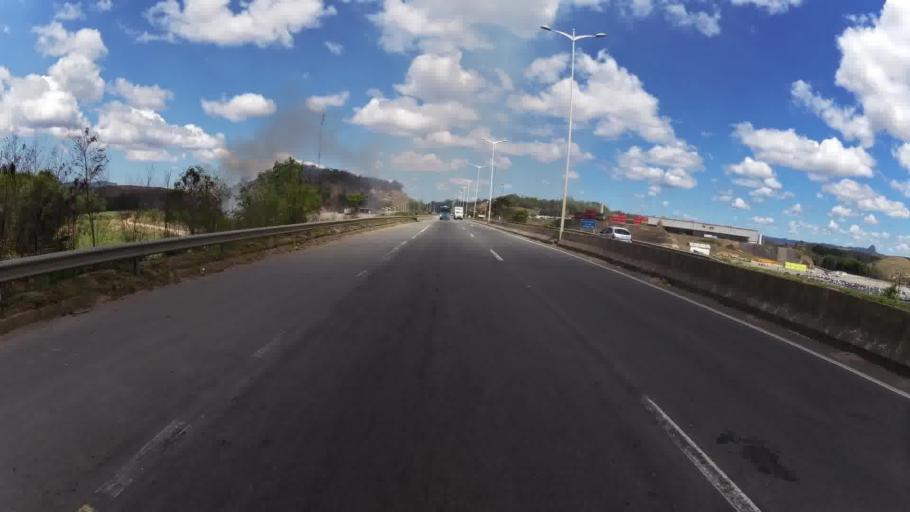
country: BR
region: Espirito Santo
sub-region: Vitoria
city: Vitoria
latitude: -20.2294
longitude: -40.3666
